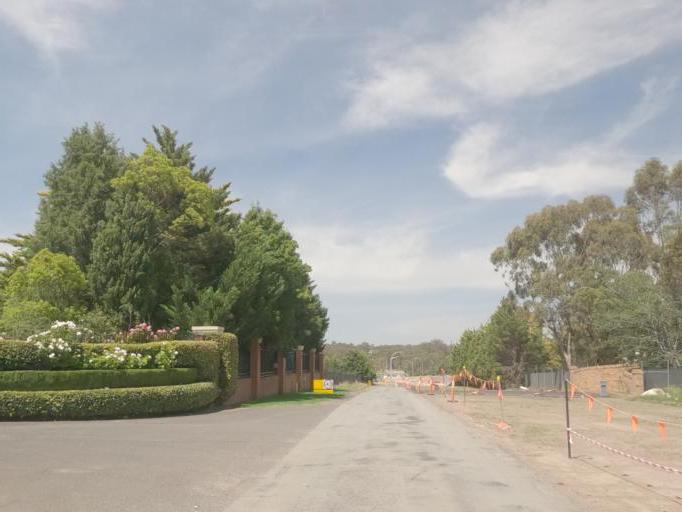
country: AU
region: Victoria
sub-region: Hume
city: Greenvale
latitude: -37.6393
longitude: 144.8751
